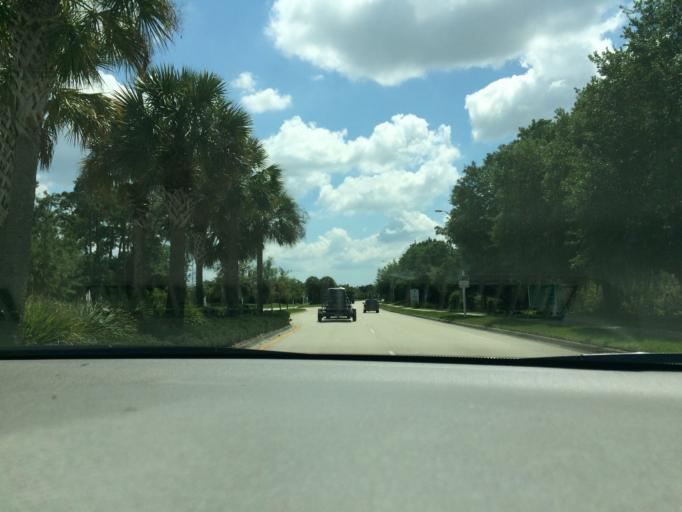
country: US
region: Florida
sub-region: Sarasota County
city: The Meadows
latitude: 27.4299
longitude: -82.3955
